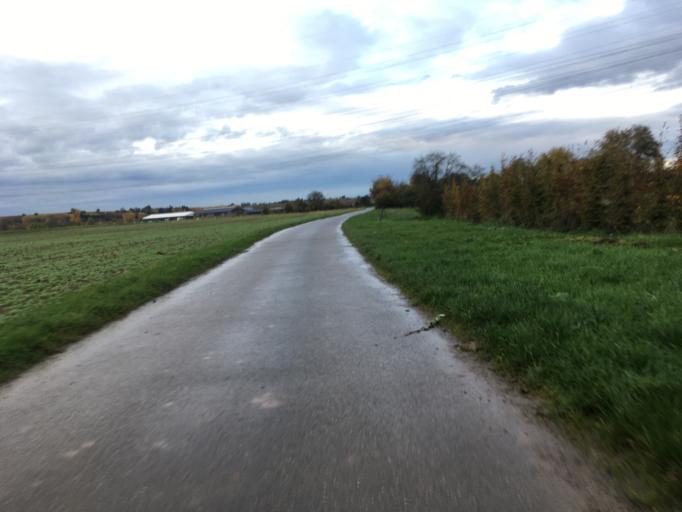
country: DE
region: Baden-Wuerttemberg
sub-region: Regierungsbezirk Stuttgart
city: Nordheim
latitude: 49.1064
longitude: 9.1609
